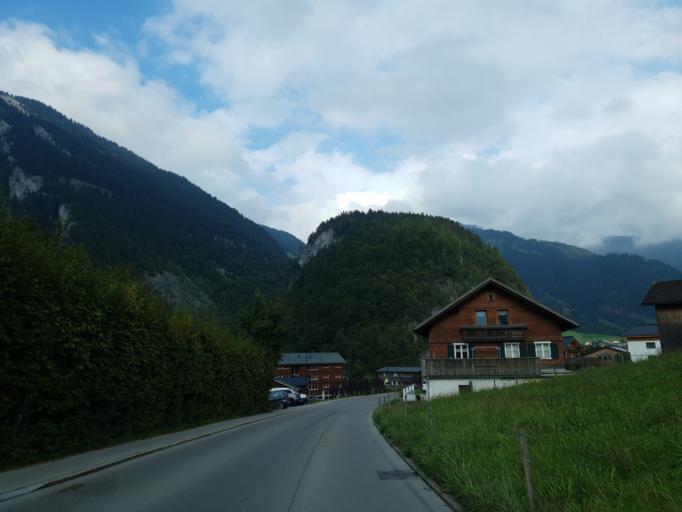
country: AT
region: Vorarlberg
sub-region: Politischer Bezirk Bregenz
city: Au
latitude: 47.3217
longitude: 9.9742
